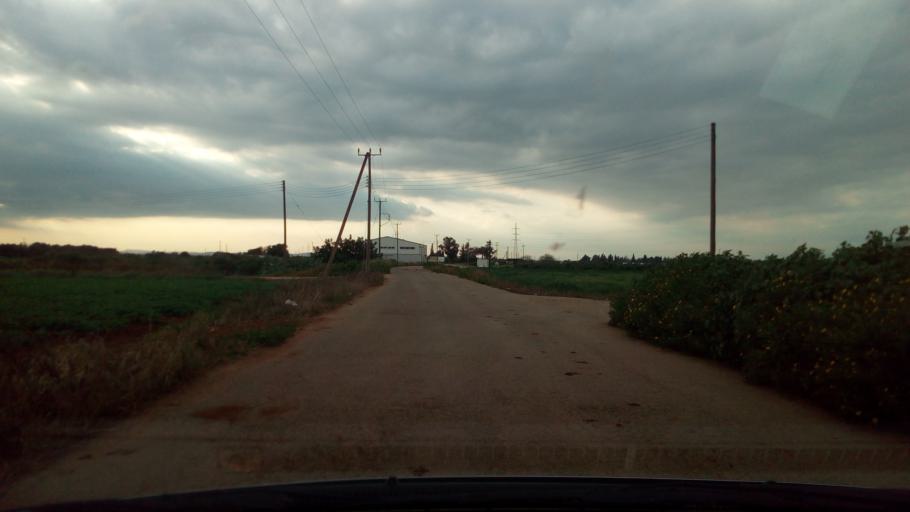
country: CY
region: Ammochostos
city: Avgorou
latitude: 34.9962
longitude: 33.8225
